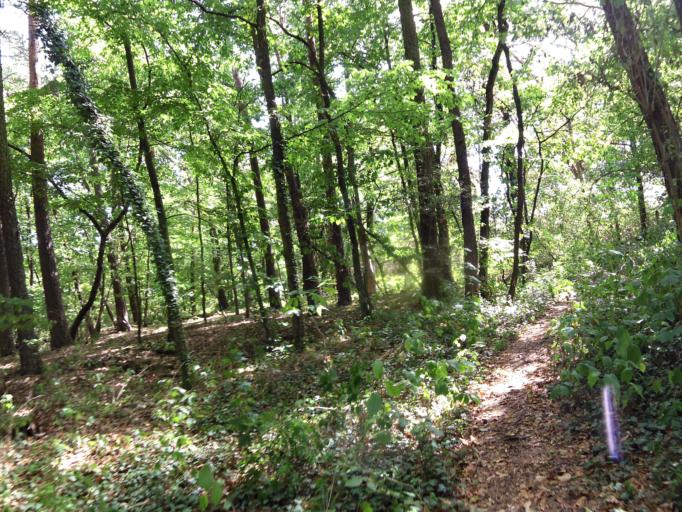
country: DE
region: Bavaria
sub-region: Regierungsbezirk Unterfranken
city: Eibelstadt
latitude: 49.7425
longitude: 10.0112
